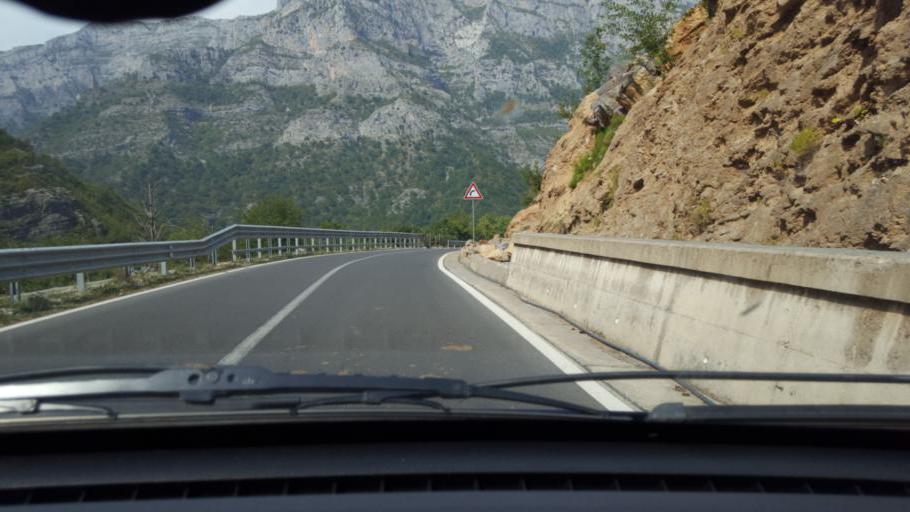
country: AL
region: Shkoder
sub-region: Rrethi i Malesia e Madhe
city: Kastrat
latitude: 42.4173
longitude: 19.5101
